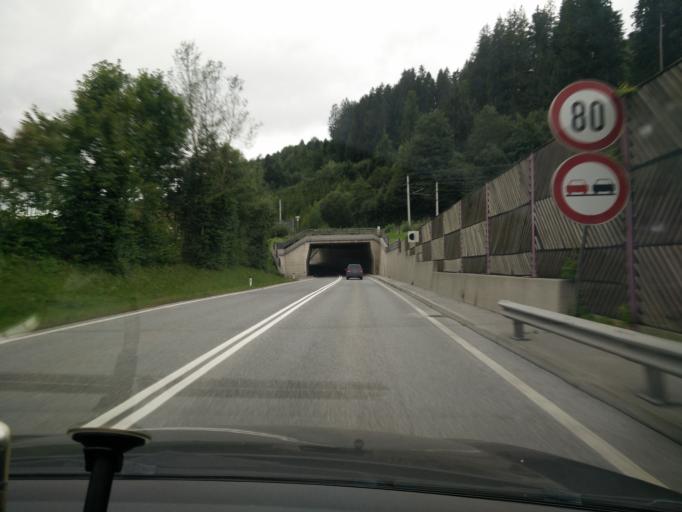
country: AT
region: Tyrol
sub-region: Politischer Bezirk Kitzbuhel
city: Kirchberg in Tirol
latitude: 47.4510
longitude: 12.3245
